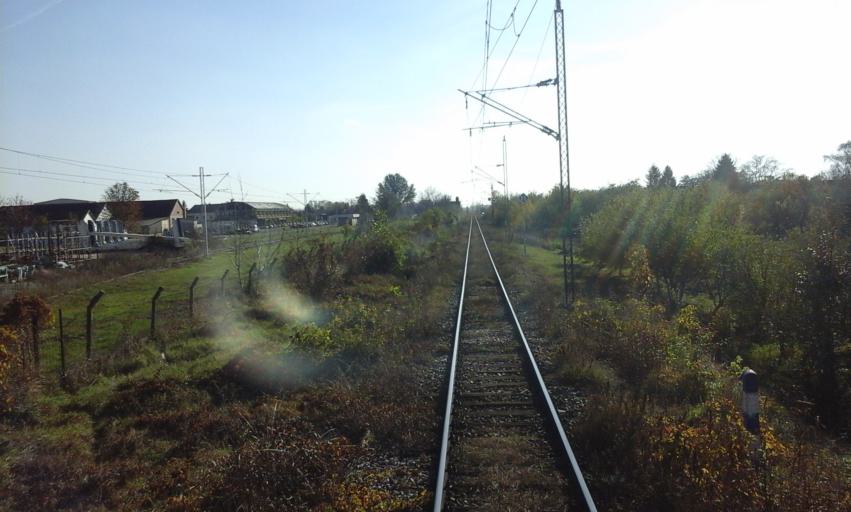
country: RS
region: Autonomna Pokrajina Vojvodina
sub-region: Severnobacki Okrug
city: Backa Topola
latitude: 45.8084
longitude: 19.6481
